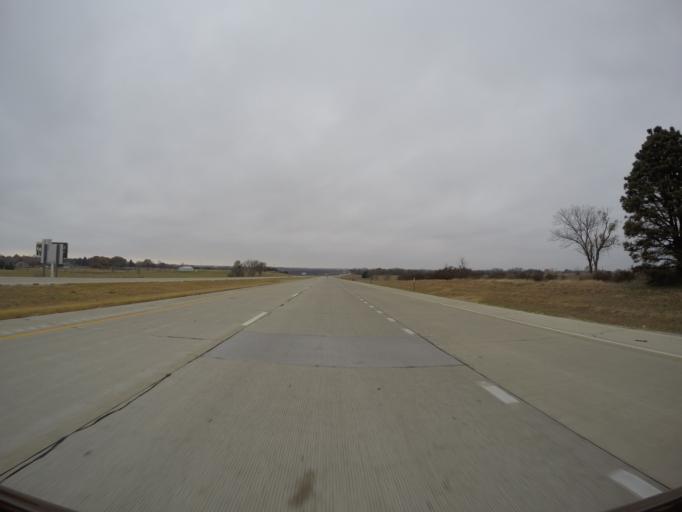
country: US
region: Kansas
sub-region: Dickinson County
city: Abilene
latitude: 38.9395
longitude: -97.2182
